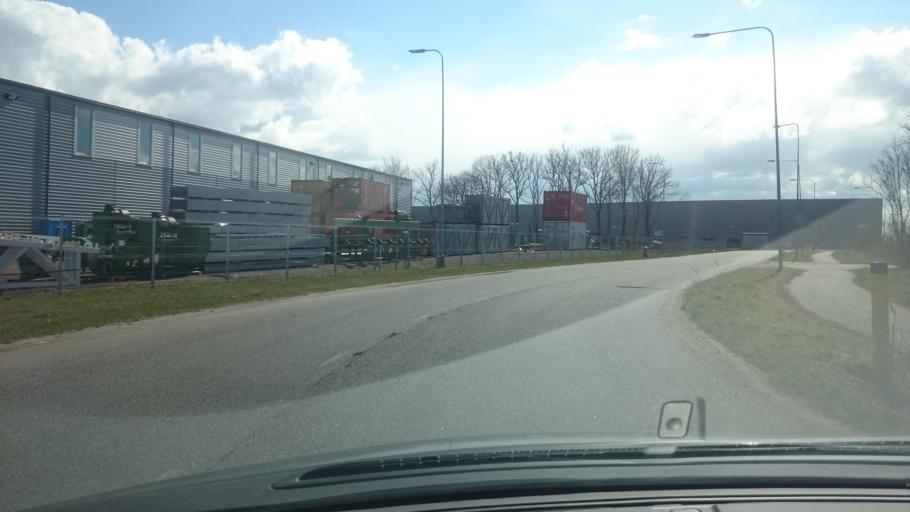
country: EE
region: Harju
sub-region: Rae vald
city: Jueri
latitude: 59.3638
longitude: 24.8735
